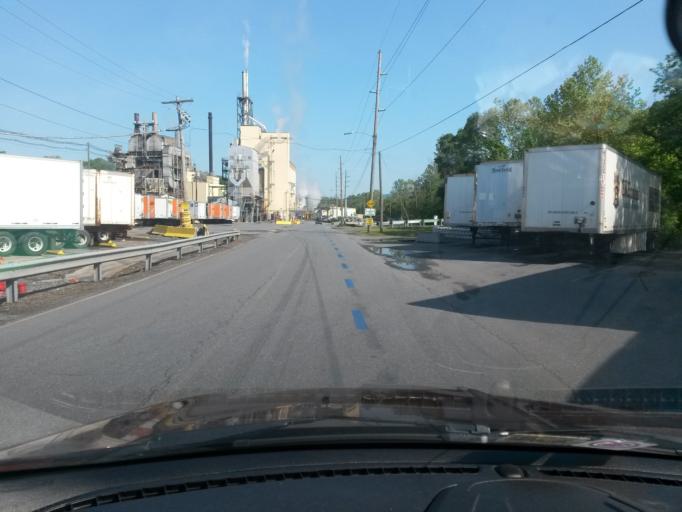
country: US
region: Virginia
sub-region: Rockbridge County
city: Glasgow
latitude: 37.5319
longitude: -79.3540
